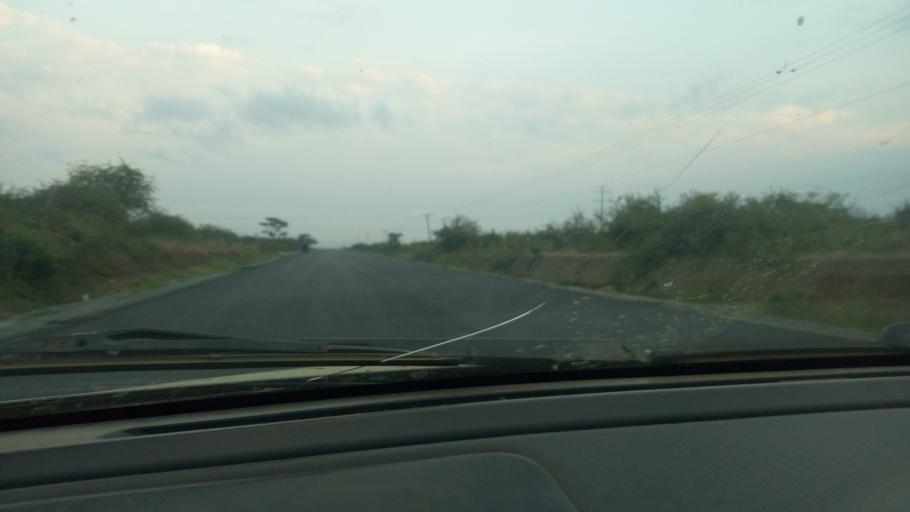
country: UG
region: Western Region
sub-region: Rubirizi District
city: Rubirizi
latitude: -0.1534
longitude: 30.0706
